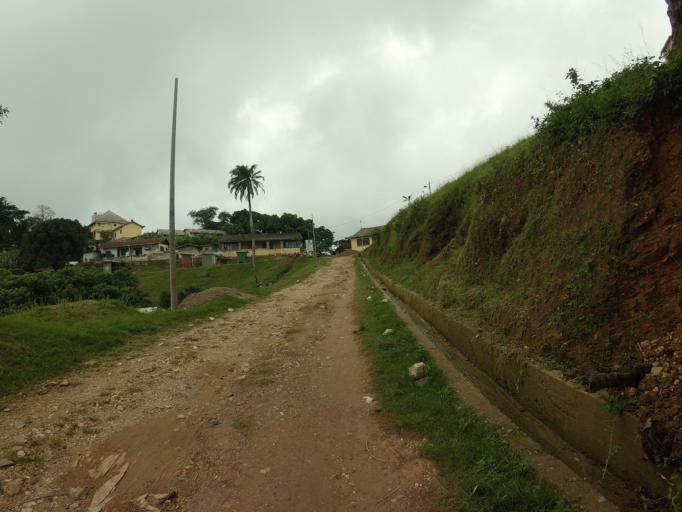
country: TG
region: Plateaux
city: Kpalime
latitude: 6.8438
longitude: 0.4366
